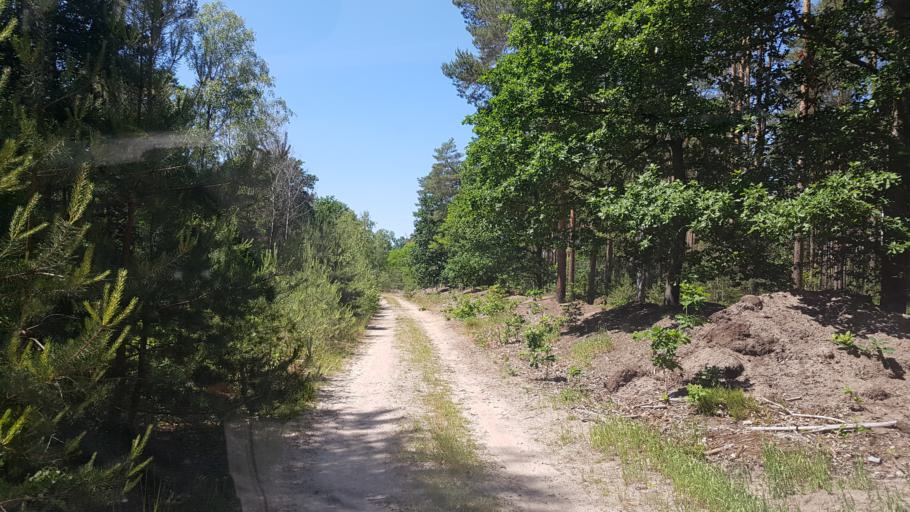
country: DE
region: Brandenburg
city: Hohenleipisch
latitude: 51.5452
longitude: 13.5394
